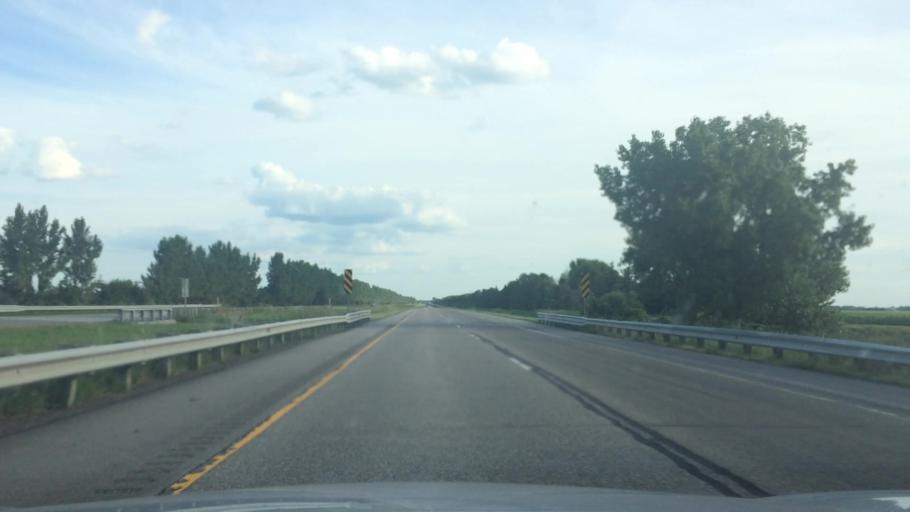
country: US
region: Wisconsin
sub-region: Portage County
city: Plover
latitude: 44.3604
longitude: -89.5209
